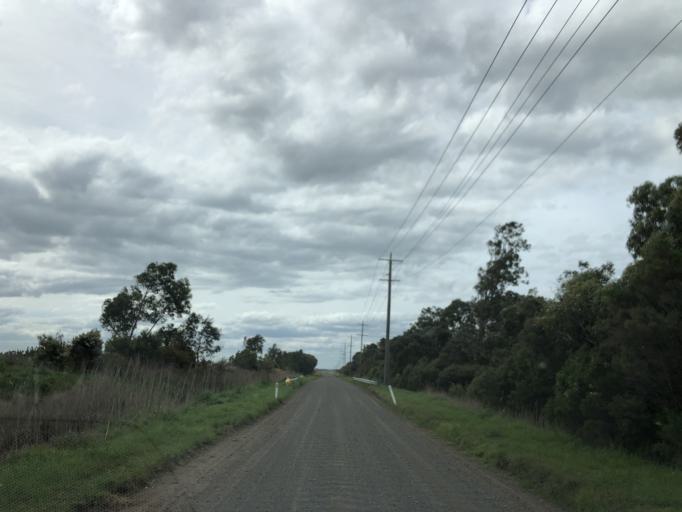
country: AU
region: Victoria
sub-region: Frankston
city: Carrum Downs
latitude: -38.0793
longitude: 145.1650
